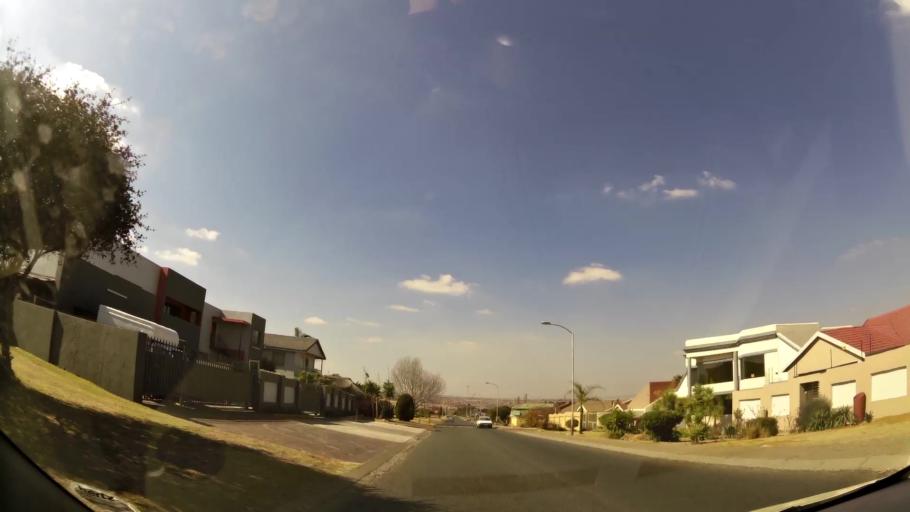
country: ZA
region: Gauteng
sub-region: West Rand District Municipality
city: Randfontein
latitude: -26.1698
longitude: 27.7520
